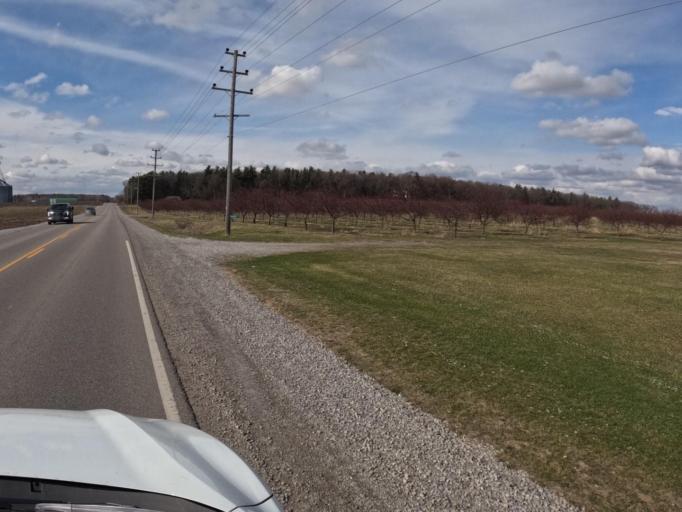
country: CA
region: Ontario
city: Norfolk County
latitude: 42.8656
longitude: -80.2681
